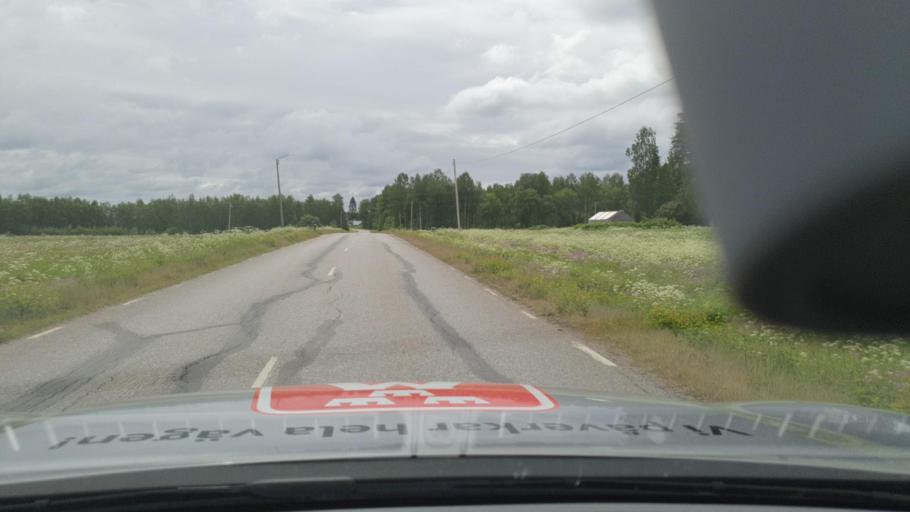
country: SE
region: Norrbotten
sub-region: Lulea Kommun
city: Ranea
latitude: 65.9229
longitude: 22.1478
